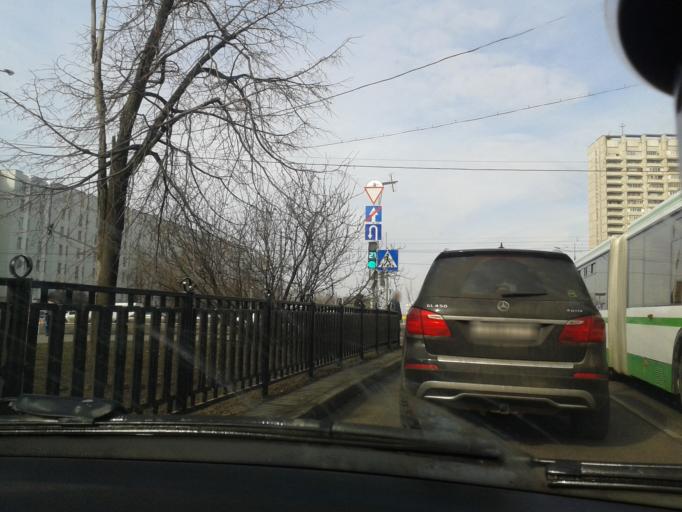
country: RU
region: Moscow
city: Strogino
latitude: 55.8057
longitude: 37.3950
